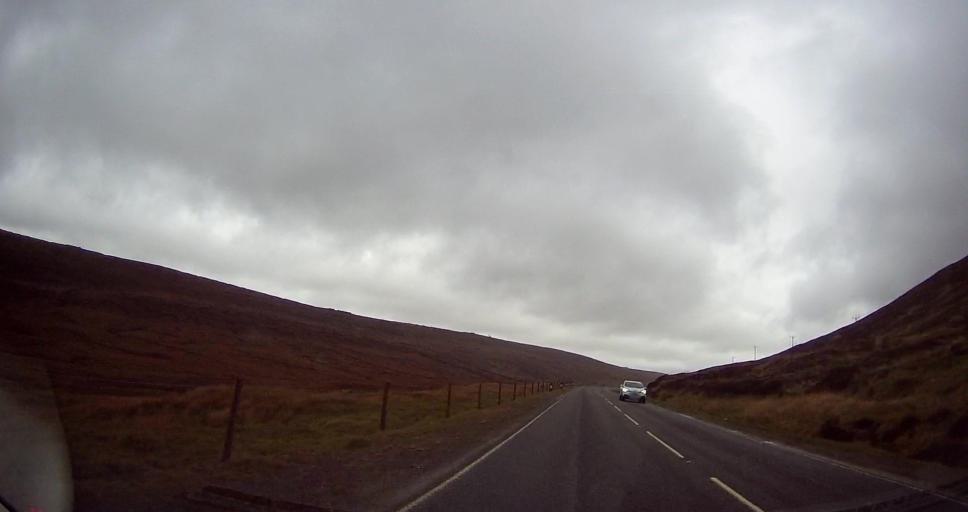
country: GB
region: Scotland
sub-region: Shetland Islands
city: Lerwick
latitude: 60.3068
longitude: -1.2419
